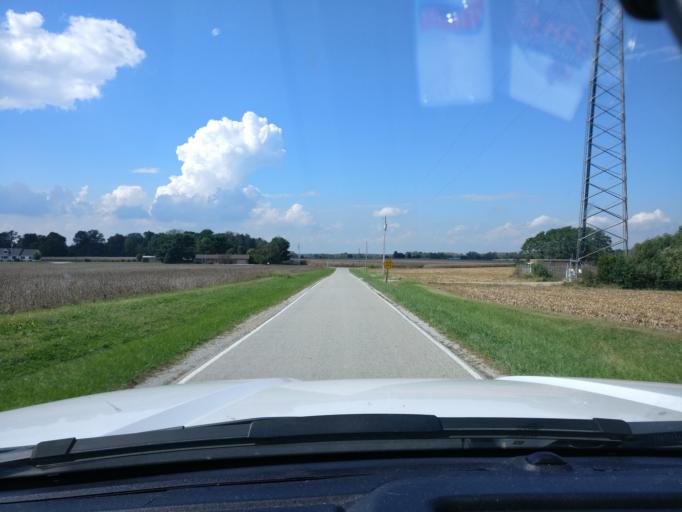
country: US
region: Ohio
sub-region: Warren County
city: Waynesville
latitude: 39.4647
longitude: -83.9917
